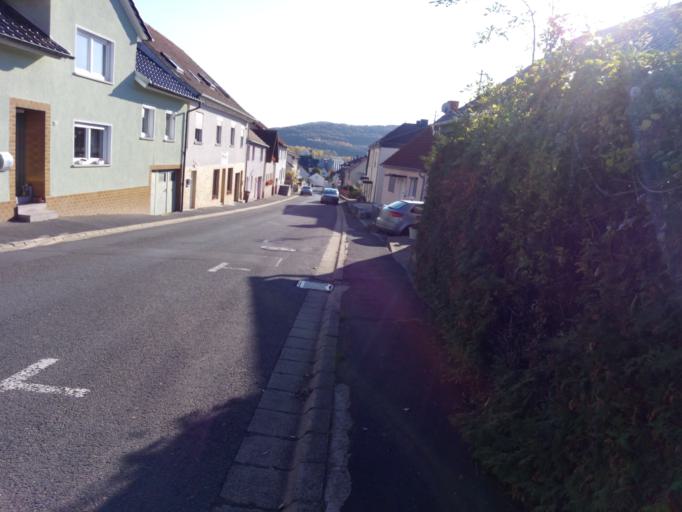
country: DE
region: Rheinland-Pfalz
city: Monzingen
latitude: 49.7979
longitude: 7.5921
